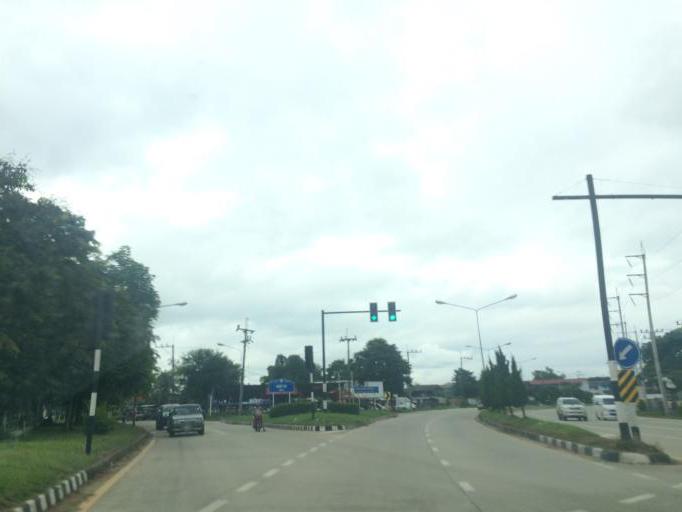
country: TH
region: Chiang Rai
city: Mae Chan
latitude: 20.1377
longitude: 99.8572
